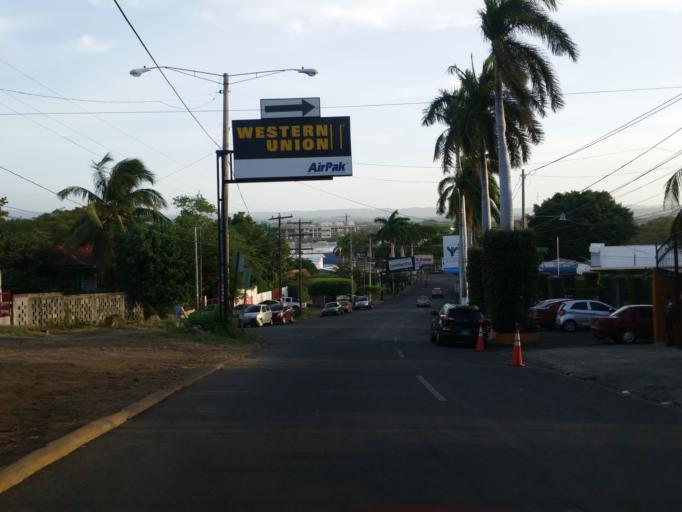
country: NI
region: Managua
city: Managua
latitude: 12.1387
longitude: -86.2757
